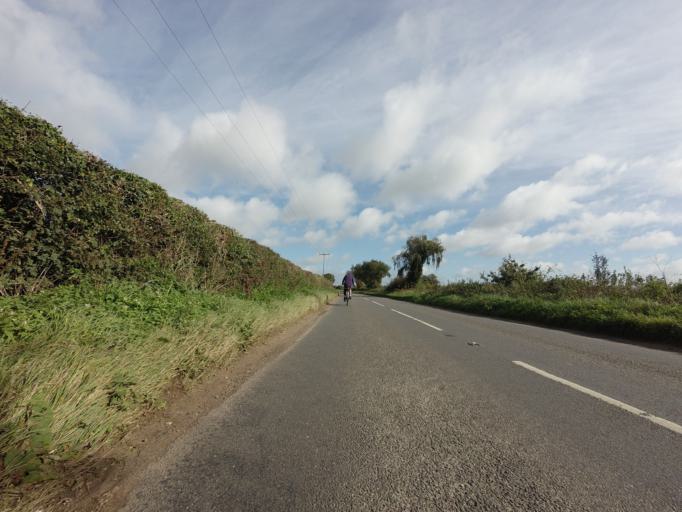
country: GB
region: England
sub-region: Norfolk
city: Wells-next-the-Sea
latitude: 52.9025
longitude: 0.6880
